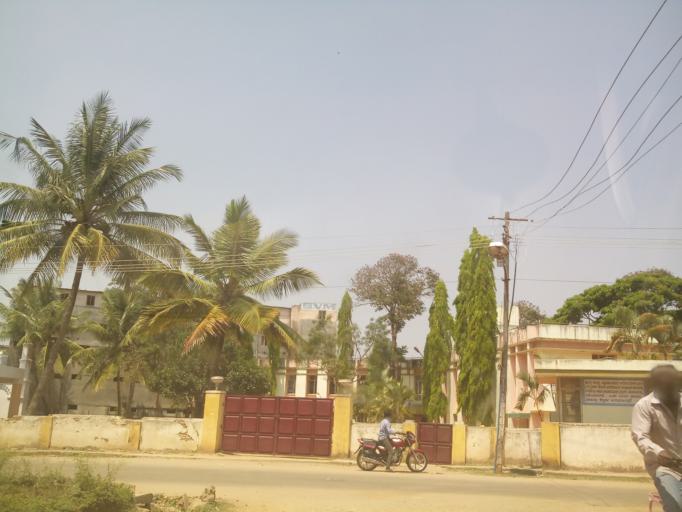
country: IN
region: Karnataka
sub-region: Hassan
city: Hassan
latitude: 13.0123
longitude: 76.0966
